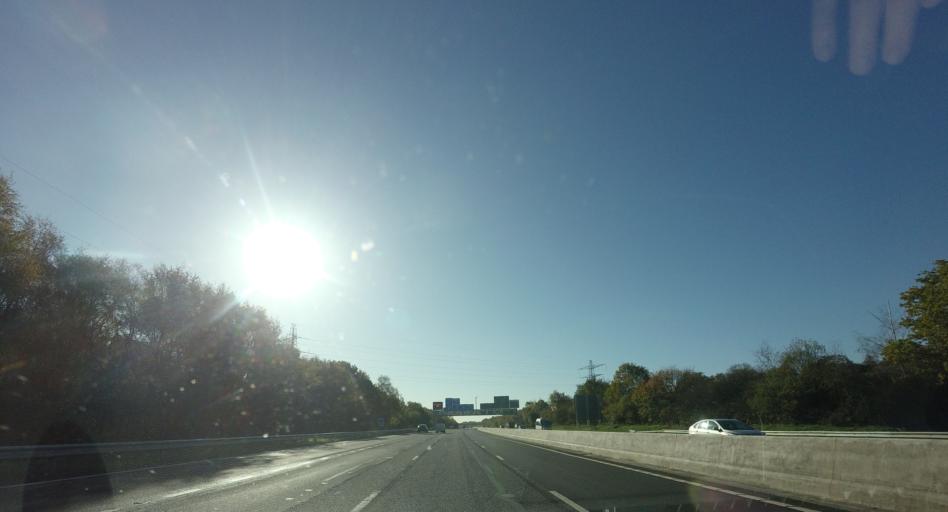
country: GB
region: England
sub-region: West Sussex
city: Copthorne
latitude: 51.1434
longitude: -0.1374
